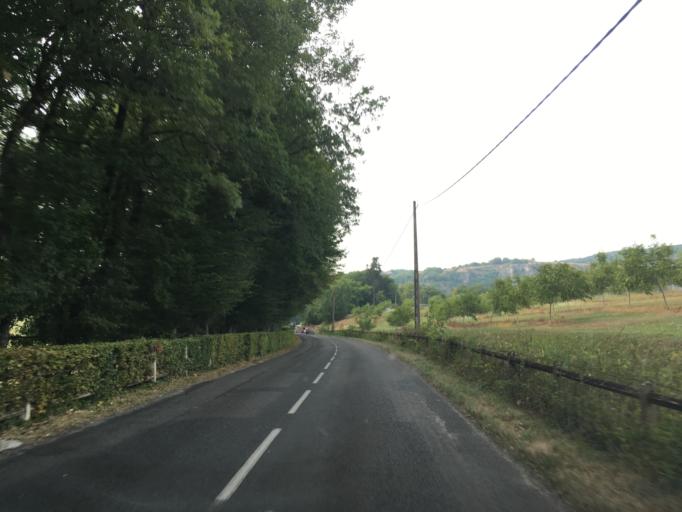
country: FR
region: Midi-Pyrenees
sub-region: Departement du Lot
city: Souillac
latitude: 44.8496
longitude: 1.5303
